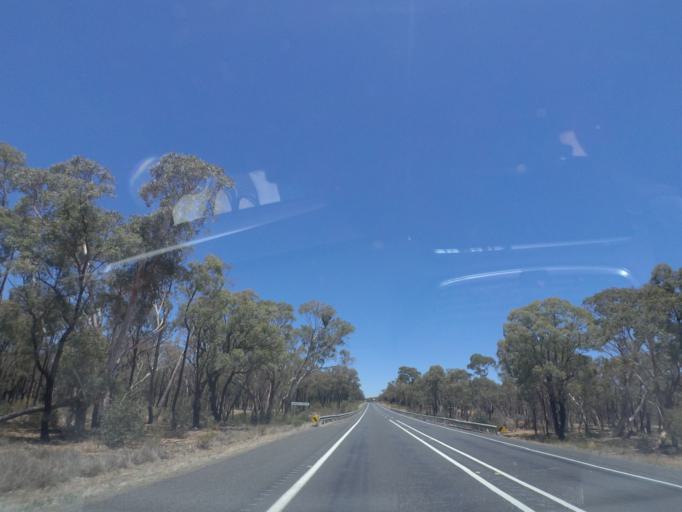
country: AU
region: New South Wales
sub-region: Warrumbungle Shire
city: Coonabarabran
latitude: -30.8806
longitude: 149.4464
